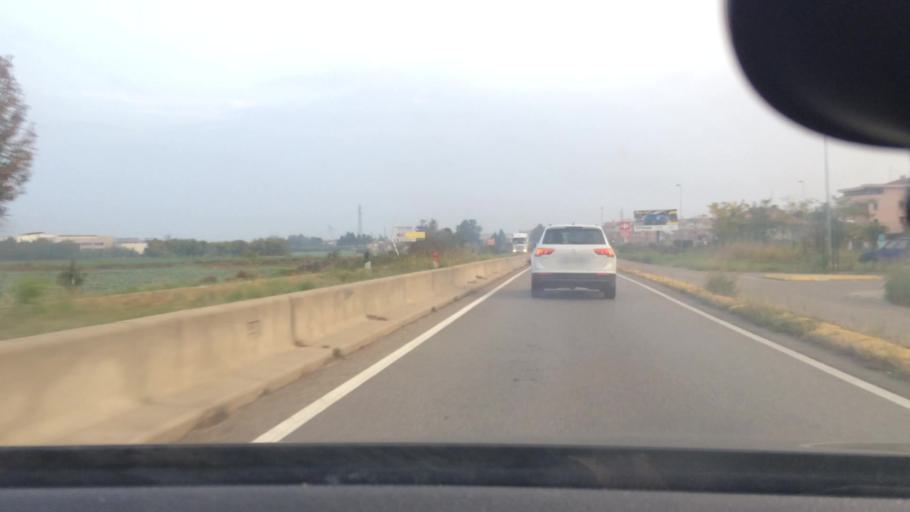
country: IT
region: Lombardy
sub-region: Citta metropolitana di Milano
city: San Giorgio Su Legnano
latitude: 45.5742
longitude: 8.9019
